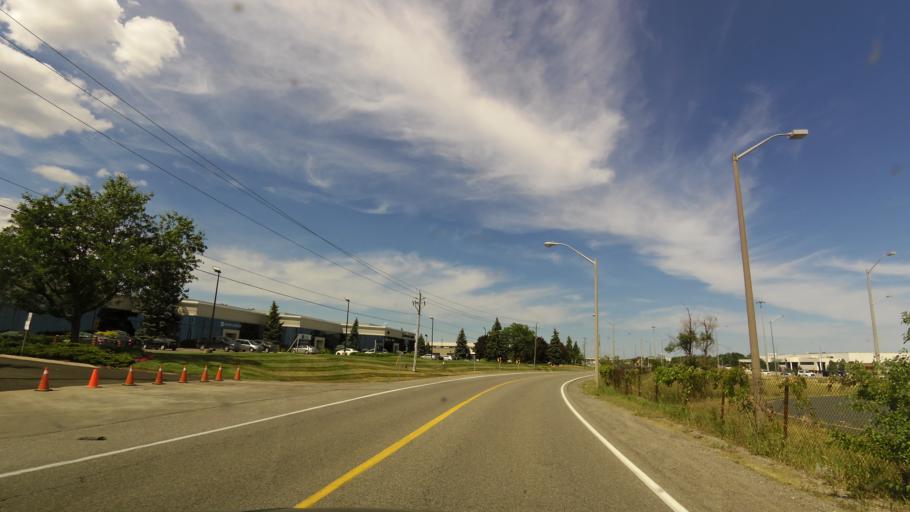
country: CA
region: Ontario
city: Oakville
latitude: 43.4348
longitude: -79.7147
